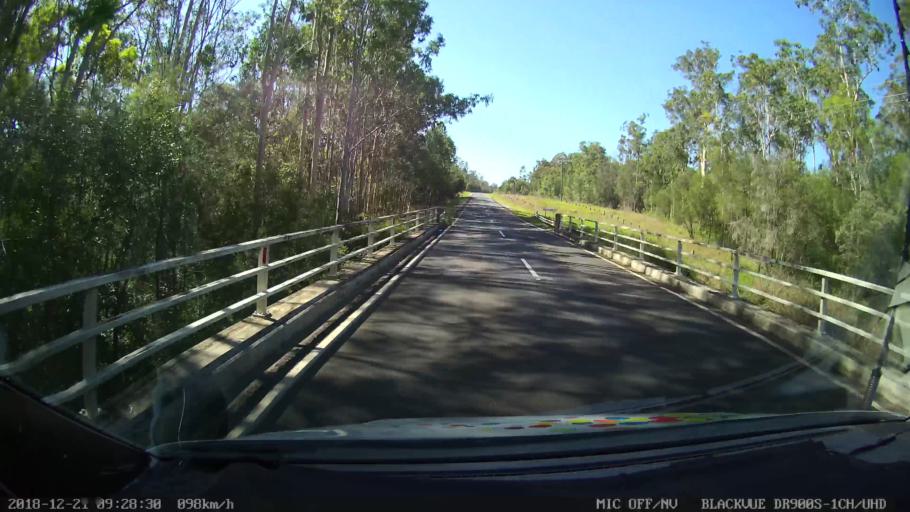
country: AU
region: New South Wales
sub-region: Clarence Valley
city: Maclean
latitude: -29.4182
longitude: 152.9870
